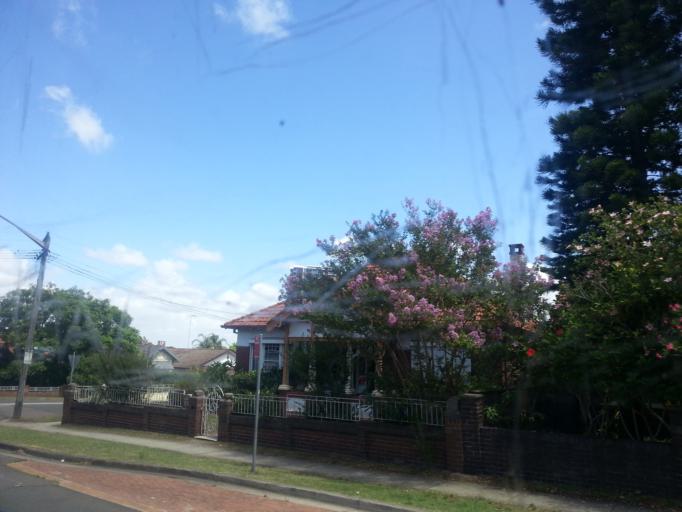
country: AU
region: New South Wales
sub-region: Randwick
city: Kensington
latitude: -33.9110
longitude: 151.2164
